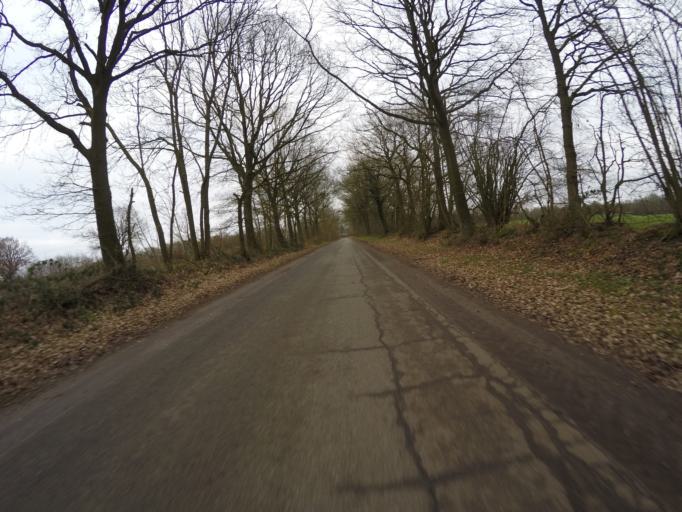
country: DE
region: Schleswig-Holstein
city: Langeln
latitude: 53.7984
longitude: 9.8710
